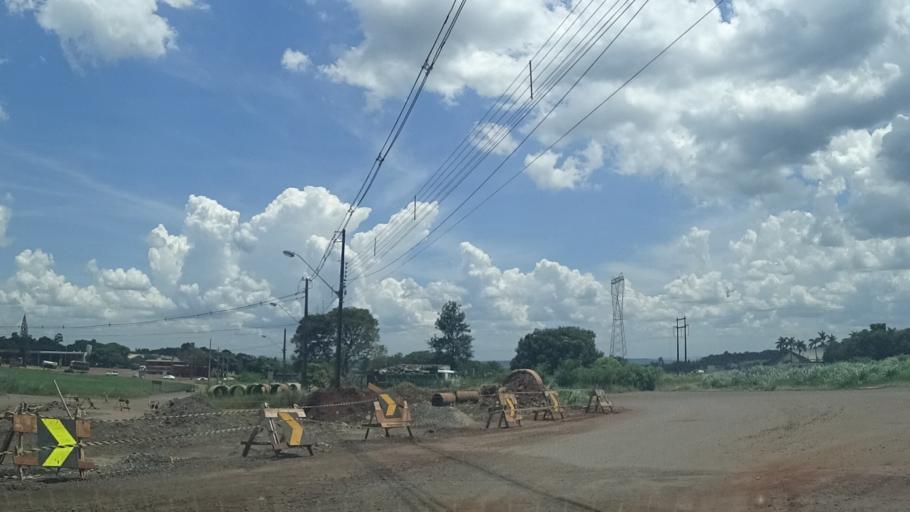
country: BR
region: Parana
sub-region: Maringa
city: Maringa
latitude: -23.4557
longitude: -51.9531
